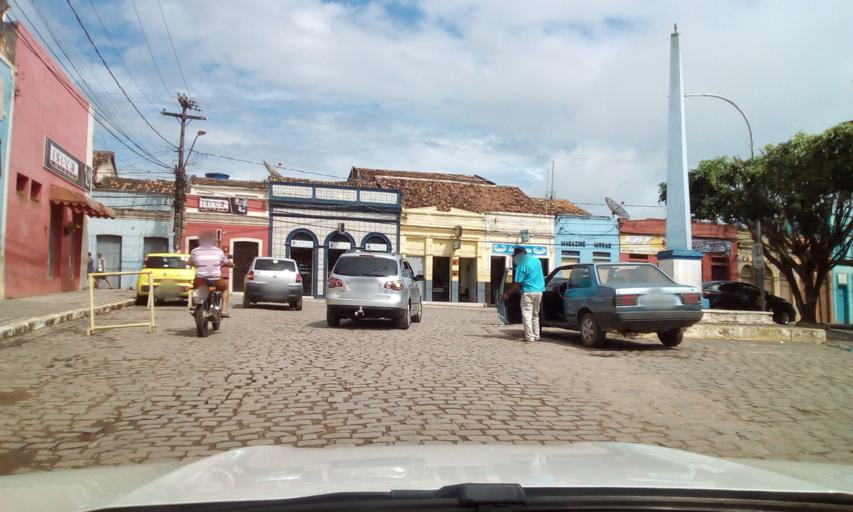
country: BR
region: Paraiba
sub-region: Areia
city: Areia
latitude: -6.9682
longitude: -35.7028
